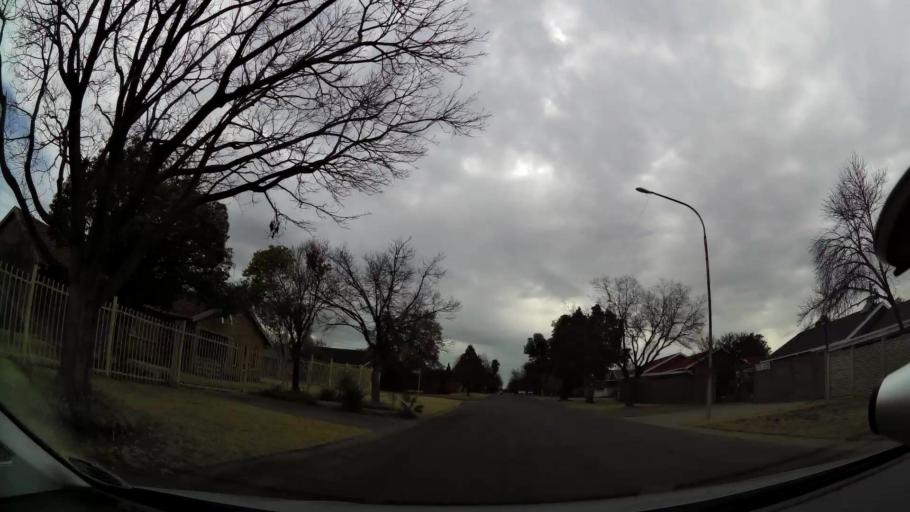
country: ZA
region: Orange Free State
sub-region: Fezile Dabi District Municipality
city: Kroonstad
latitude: -27.6351
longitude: 27.2412
